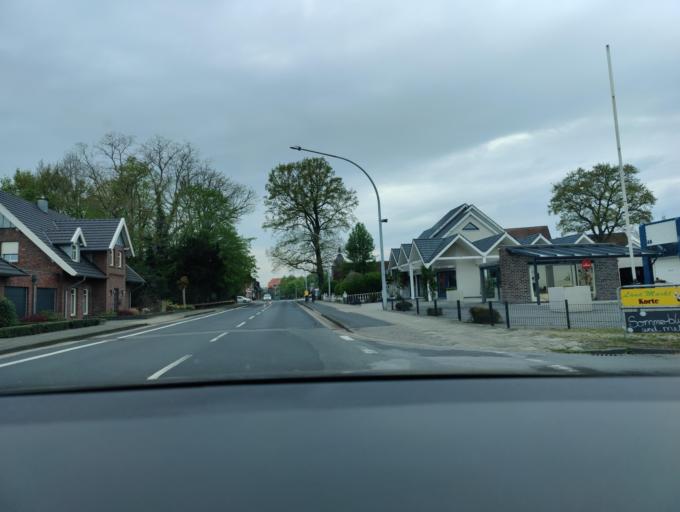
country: DE
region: Lower Saxony
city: Wietmarschen
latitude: 52.5185
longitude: 7.1358
